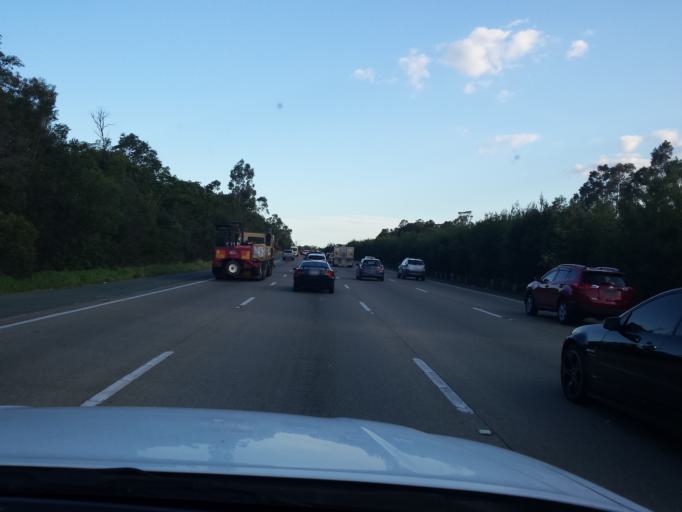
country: AU
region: Queensland
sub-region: Gold Coast
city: Oxenford
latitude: -27.8461
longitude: 153.3055
